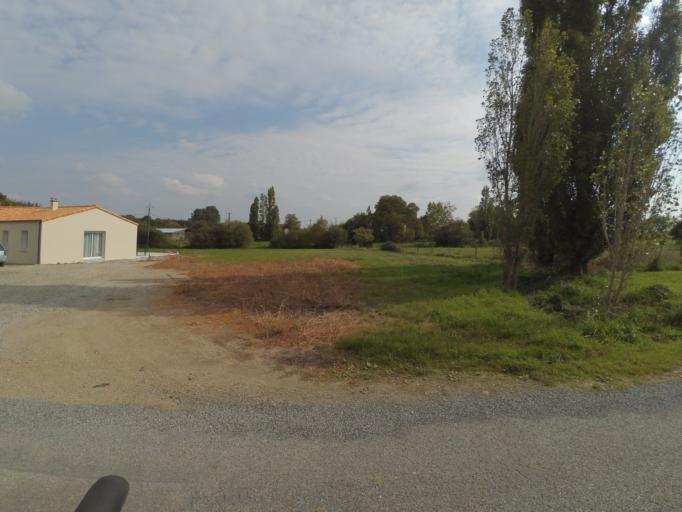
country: FR
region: Pays de la Loire
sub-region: Departement de la Loire-Atlantique
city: Vieillevigne
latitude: 46.9864
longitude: -1.4027
